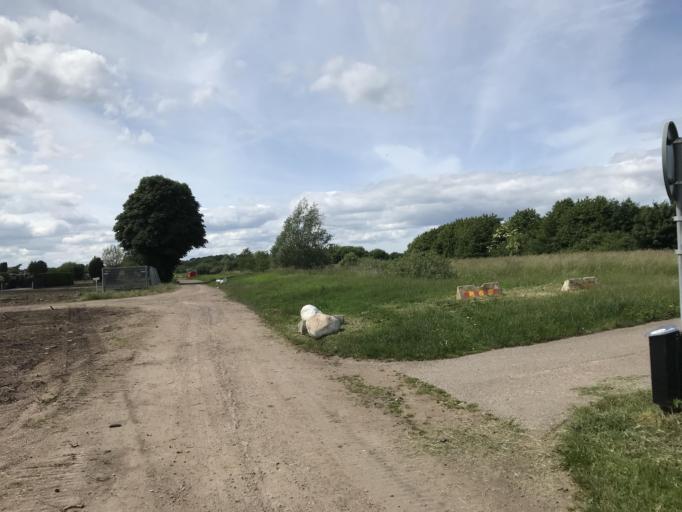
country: SE
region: Skane
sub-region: Landskrona
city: Landskrona
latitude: 55.8963
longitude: 12.8476
